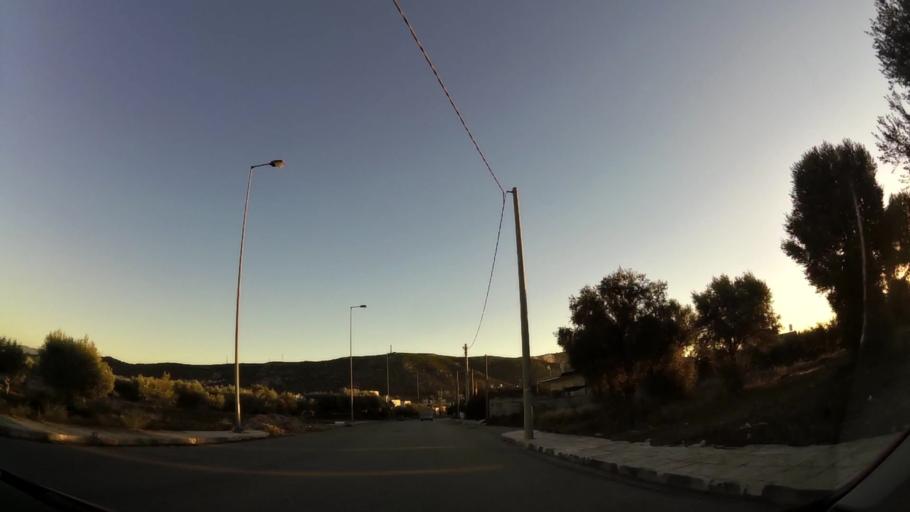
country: GR
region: Attica
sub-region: Nomarchia Dytikis Attikis
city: Ano Liosia
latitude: 38.0798
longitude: 23.6867
